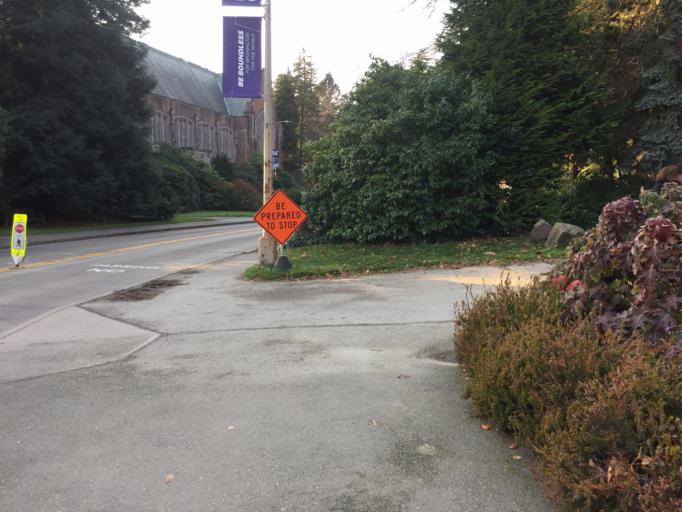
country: US
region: Washington
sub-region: King County
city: Seattle
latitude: 47.6522
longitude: -122.3069
